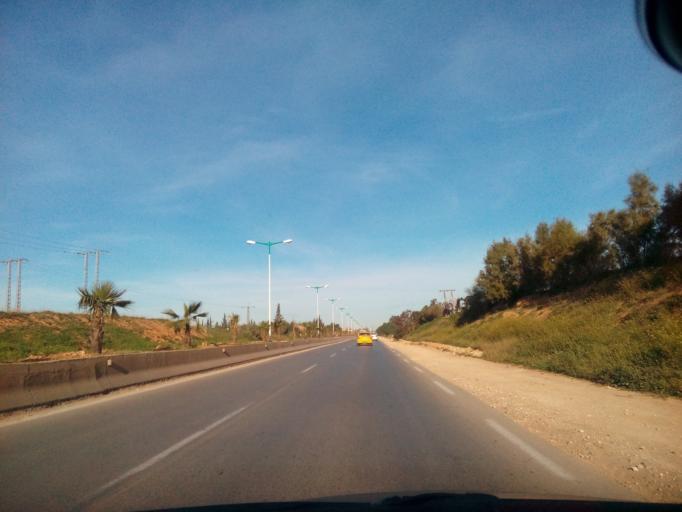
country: DZ
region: Mostaganem
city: Mostaganem
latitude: 35.8633
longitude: 0.1568
